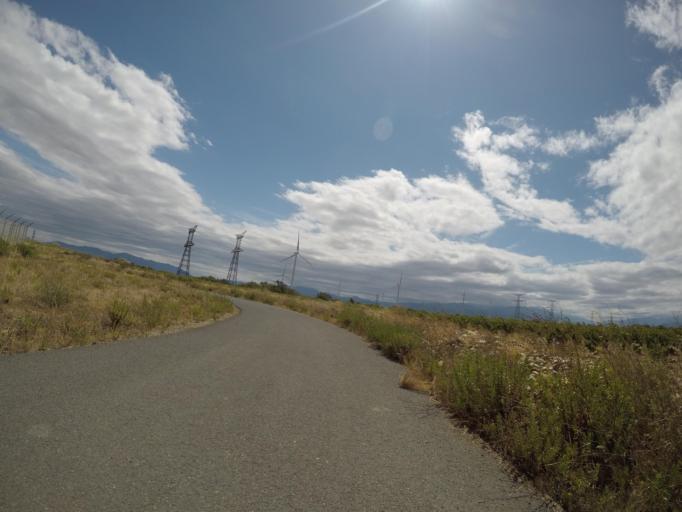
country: FR
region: Languedoc-Roussillon
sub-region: Departement des Pyrenees-Orientales
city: Baixas
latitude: 42.7306
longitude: 2.7995
